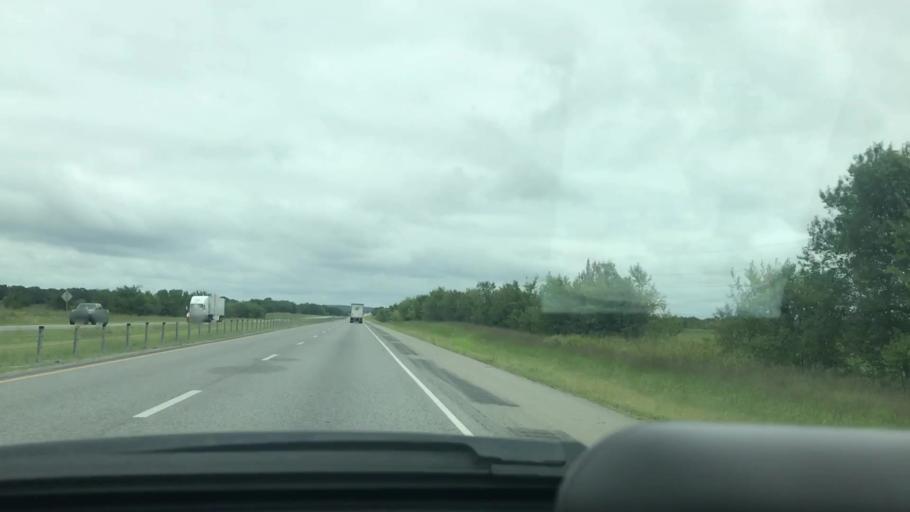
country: US
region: Oklahoma
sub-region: Pittsburg County
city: McAlester
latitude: 34.7542
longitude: -95.8928
